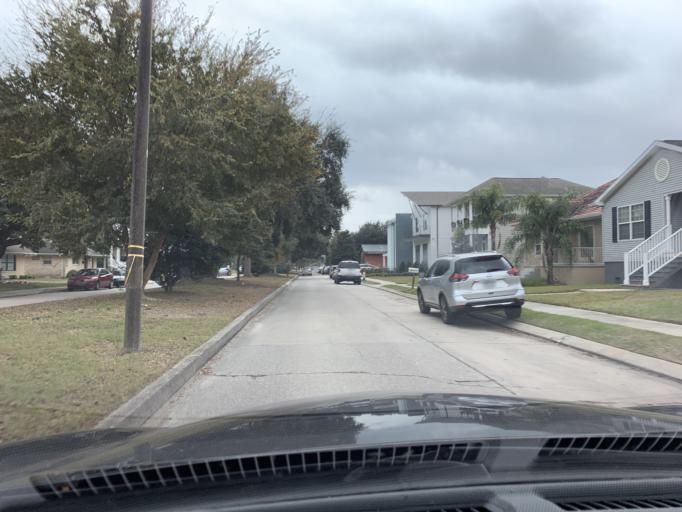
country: US
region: Louisiana
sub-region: Jefferson Parish
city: Metairie
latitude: 30.0058
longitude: -90.1026
